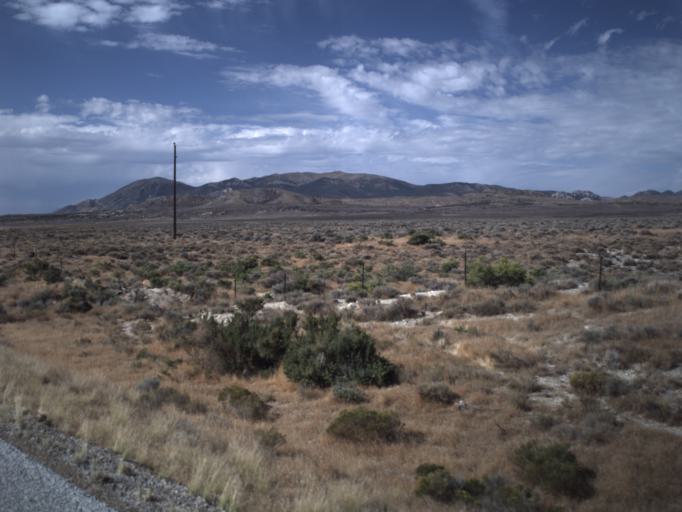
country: US
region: Utah
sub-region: Tooele County
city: Wendover
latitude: 41.5604
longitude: -113.5833
